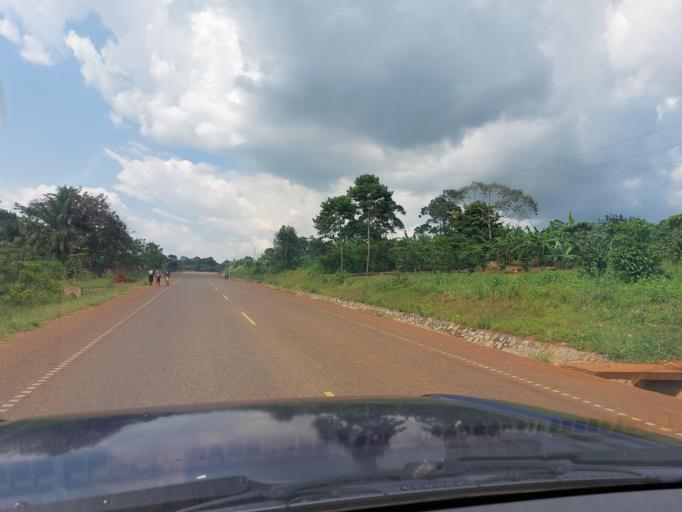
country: UG
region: Central Region
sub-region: Buikwe District
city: Buikwe
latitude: 0.3252
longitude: 33.1147
